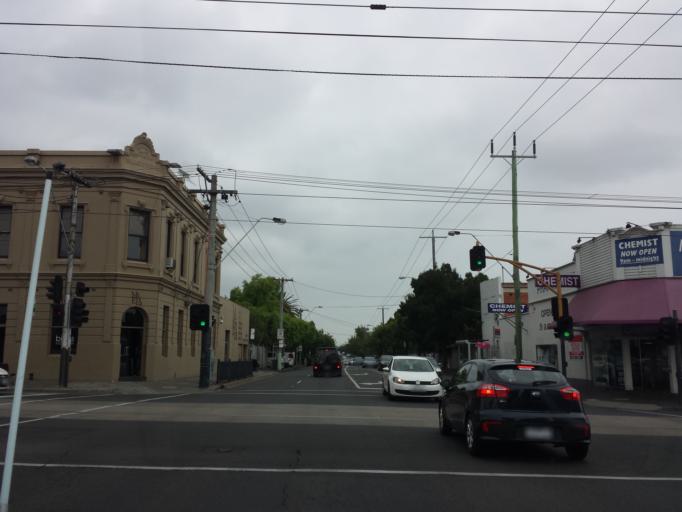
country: AU
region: Victoria
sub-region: Stonnington
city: Windsor
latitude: -37.8529
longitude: 145.0025
